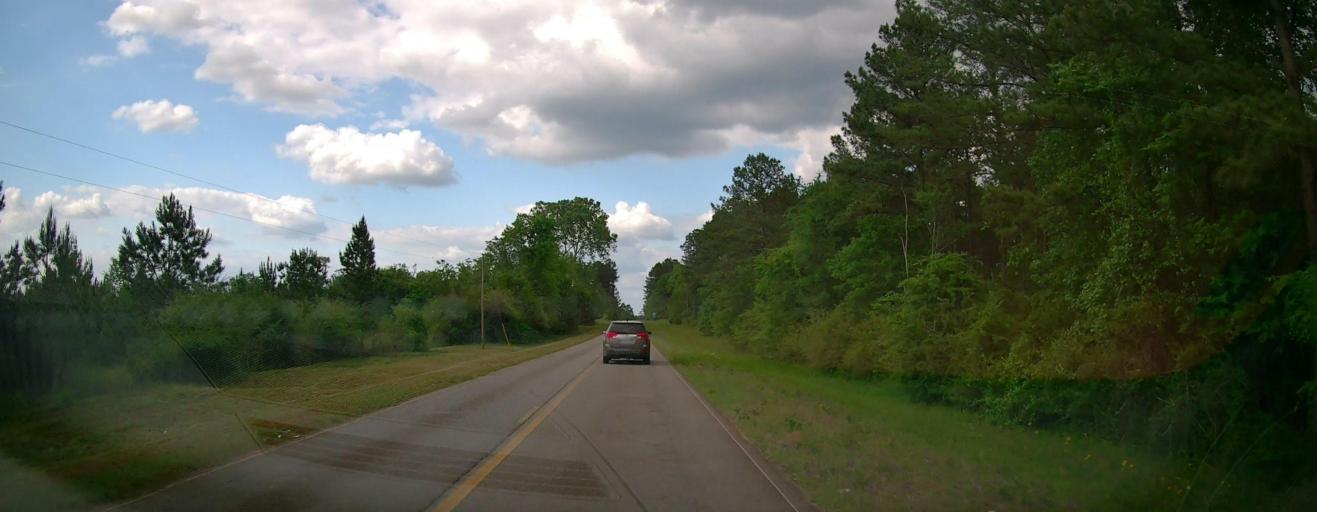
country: US
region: Georgia
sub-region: Washington County
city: Tennille
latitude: 32.7725
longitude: -82.9289
